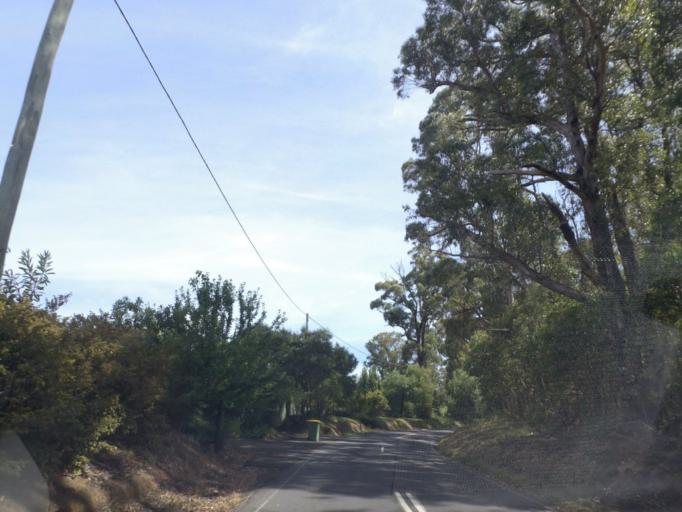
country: AU
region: Victoria
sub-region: Nillumbik
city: Saint Andrews
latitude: -37.5383
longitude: 145.3393
